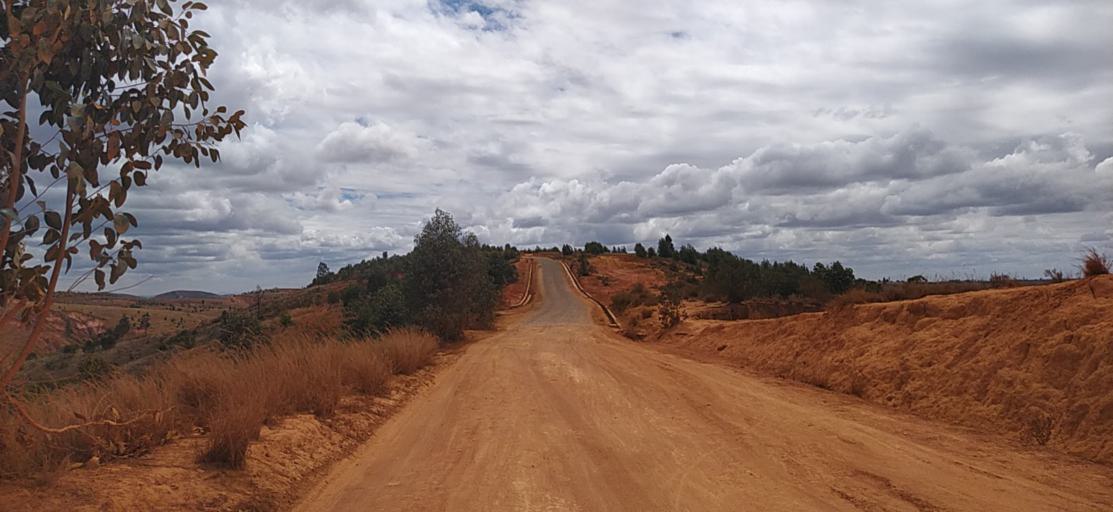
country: MG
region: Alaotra Mangoro
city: Ambatondrazaka
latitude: -18.0589
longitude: 48.2559
